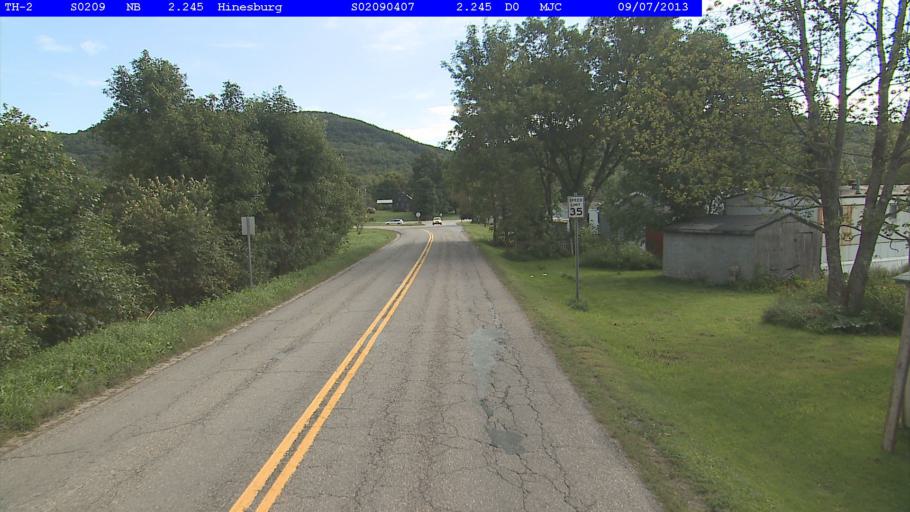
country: US
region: Vermont
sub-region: Chittenden County
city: Hinesburg
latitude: 44.3448
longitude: -73.0803
